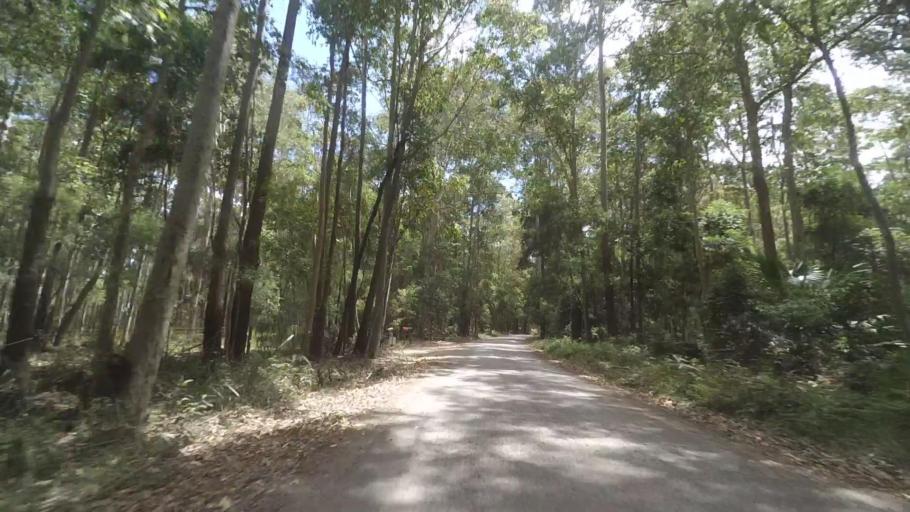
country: AU
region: New South Wales
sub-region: Shoalhaven Shire
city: Milton
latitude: -35.4434
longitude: 150.3114
